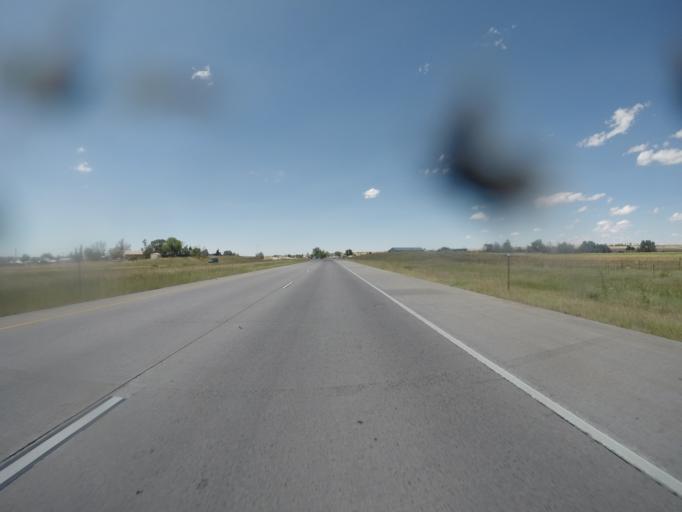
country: US
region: Colorado
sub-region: Arapahoe County
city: Byers
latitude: 39.6083
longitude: -104.0369
